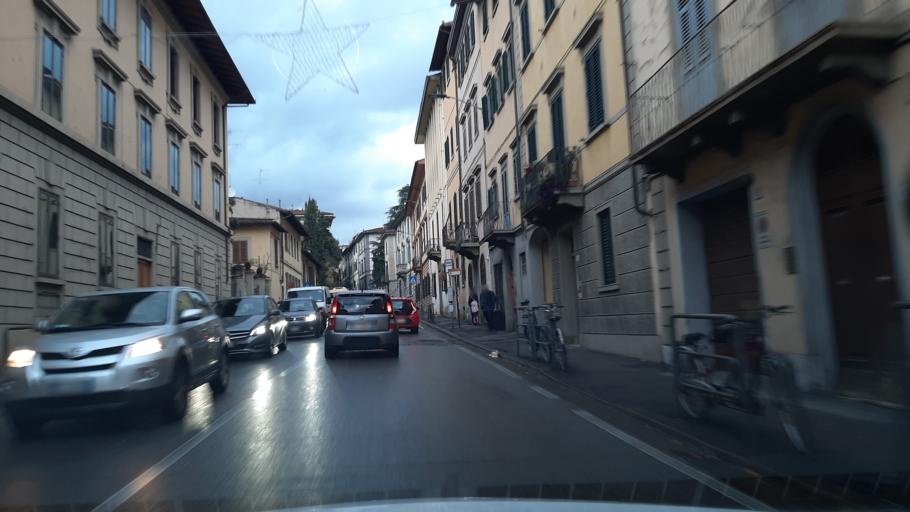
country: IT
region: Tuscany
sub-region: Province of Florence
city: Florence
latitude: 43.7870
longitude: 11.2625
